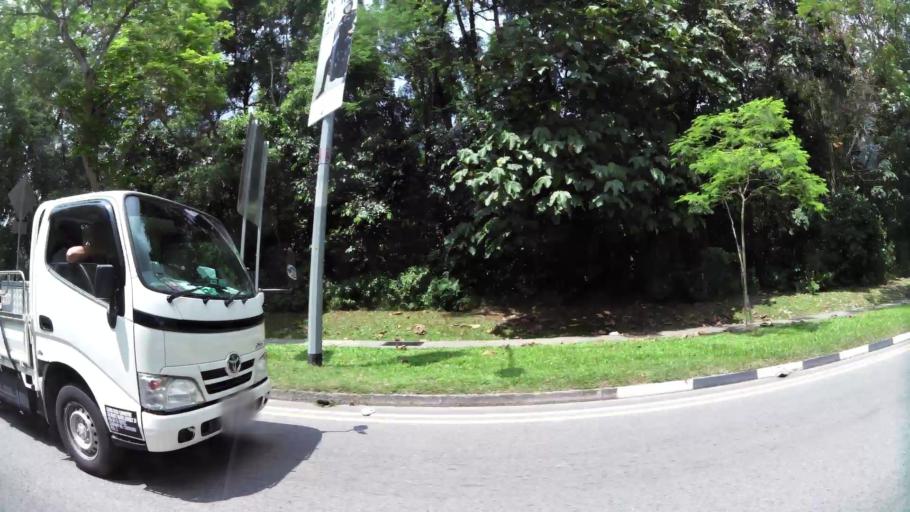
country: MY
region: Johor
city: Johor Bahru
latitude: 1.4442
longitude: 103.7888
